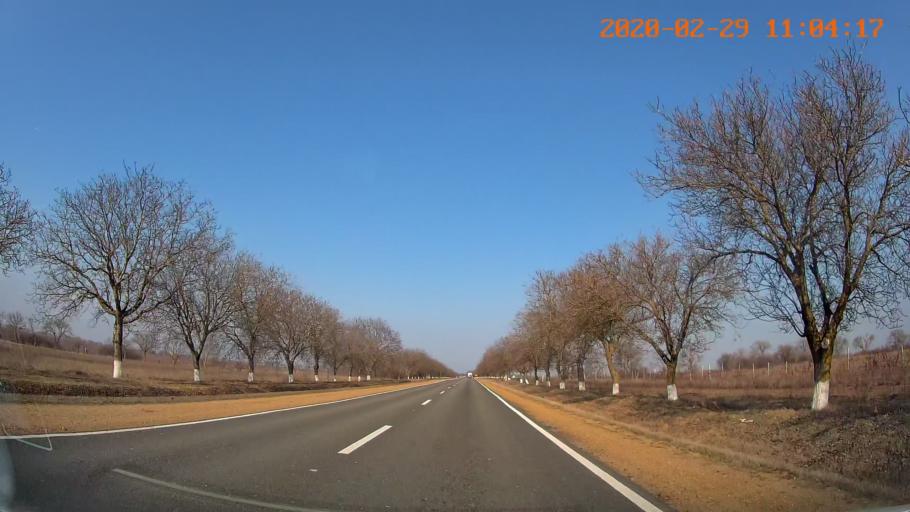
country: MD
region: Criuleni
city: Criuleni
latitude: 47.1871
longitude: 29.2042
